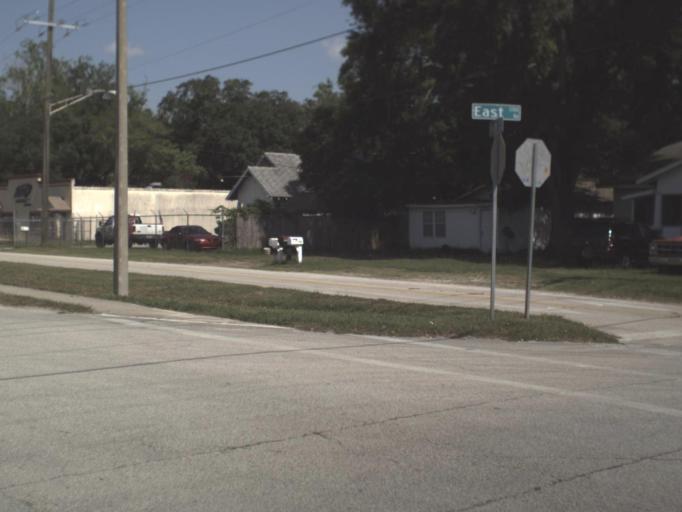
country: US
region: Florida
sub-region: Duval County
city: Jacksonville
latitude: 30.2893
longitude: -81.5846
